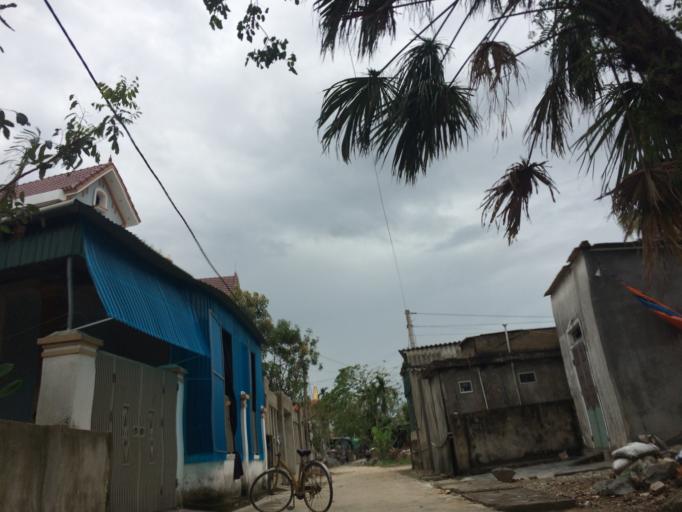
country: VN
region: Ha Tinh
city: Thach Ha
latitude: 18.3649
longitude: 105.8856
